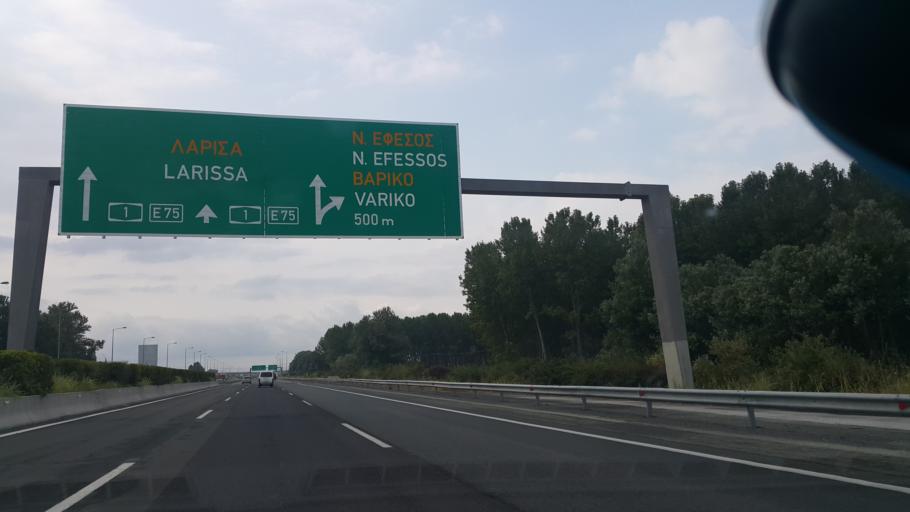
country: GR
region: Central Macedonia
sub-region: Nomos Pierias
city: Nea Efesos
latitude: 40.2026
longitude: 22.5465
